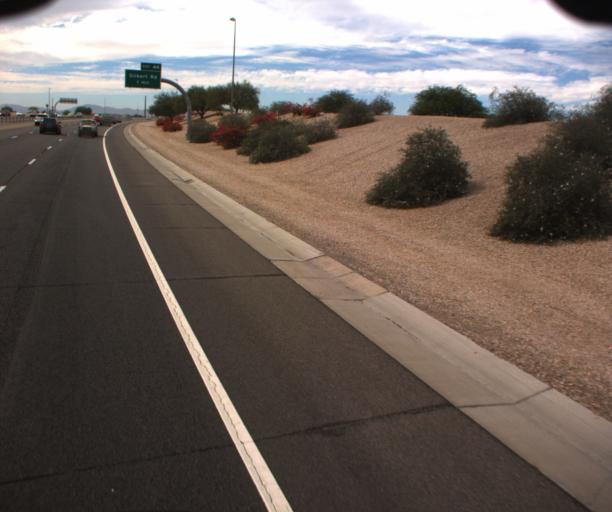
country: US
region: Arizona
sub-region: Maricopa County
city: Gilbert
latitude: 33.2838
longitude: -111.7651
